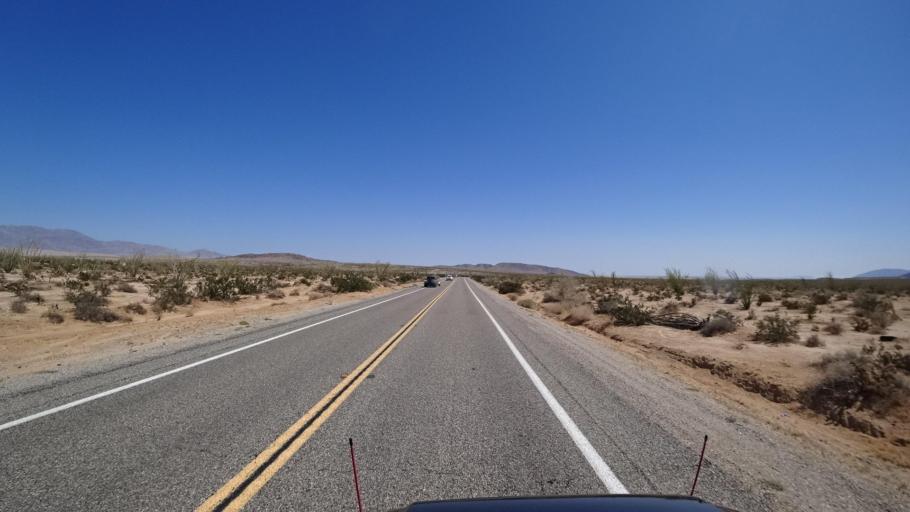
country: US
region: California
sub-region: San Diego County
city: Borrego Springs
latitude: 33.1578
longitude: -116.2428
